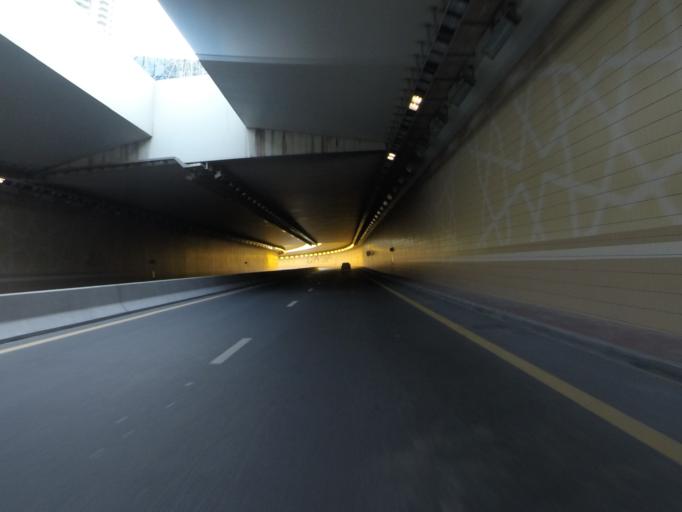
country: AE
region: Dubai
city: Dubai
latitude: 25.2003
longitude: 55.2746
